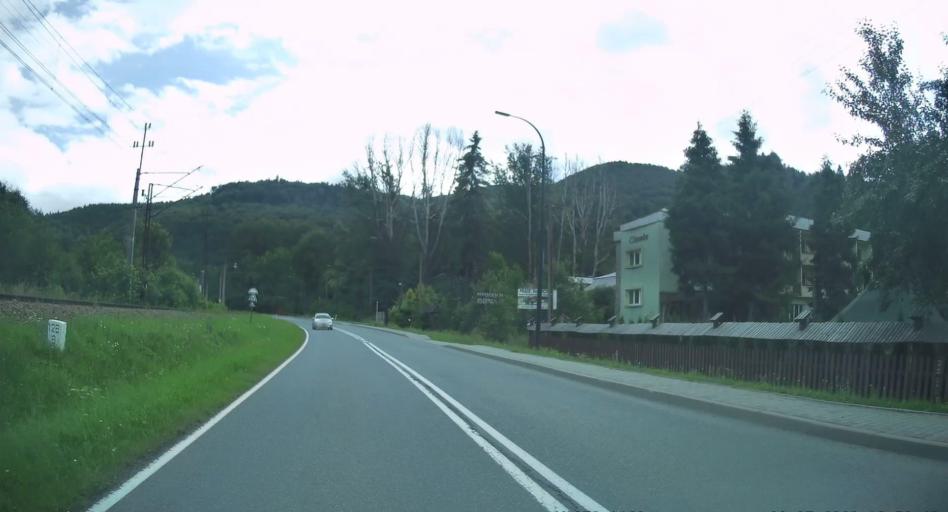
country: PL
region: Lesser Poland Voivodeship
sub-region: Powiat nowosadecki
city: Piwniczna-Zdroj
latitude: 49.3638
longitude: 20.7829
